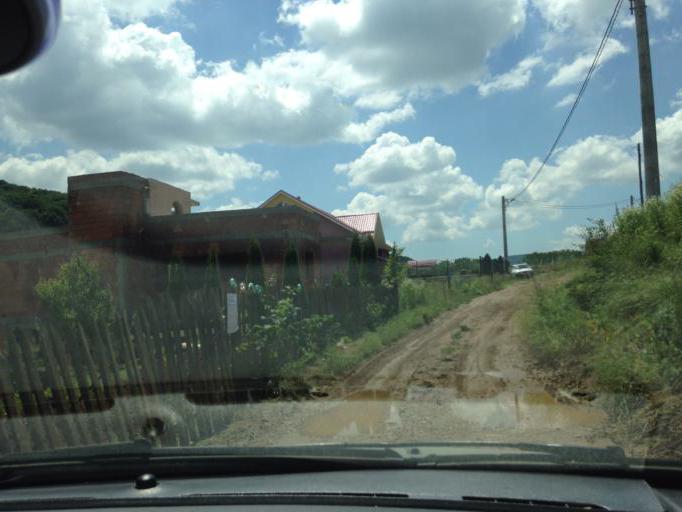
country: RO
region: Cluj
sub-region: Comuna Floresti
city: Floresti
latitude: 46.7407
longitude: 23.5326
